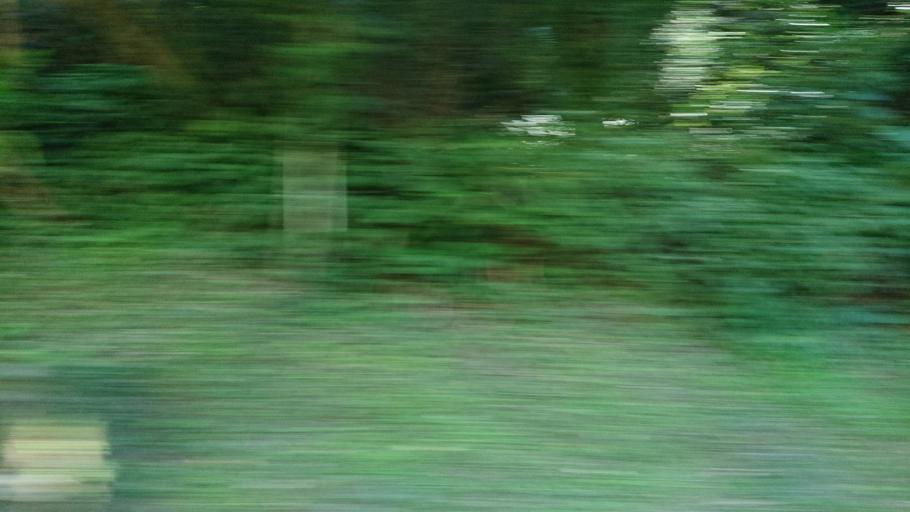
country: TW
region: Taiwan
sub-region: Yilan
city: Yilan
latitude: 24.5770
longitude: 121.4819
